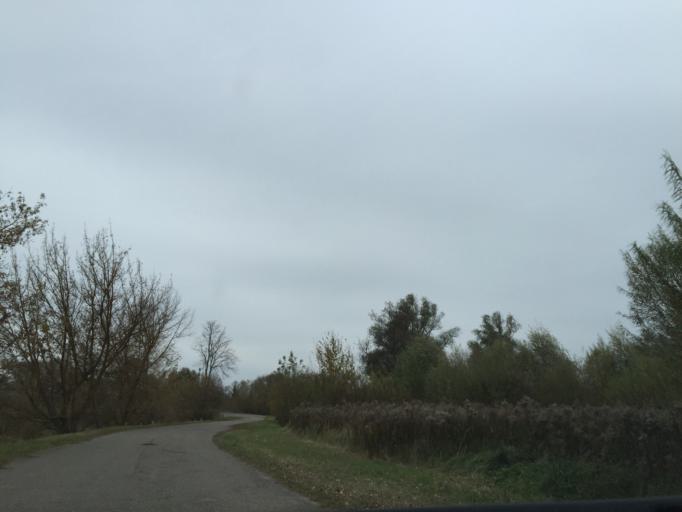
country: LV
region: Jelgava
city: Jelgava
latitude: 56.6369
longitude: 23.7408
